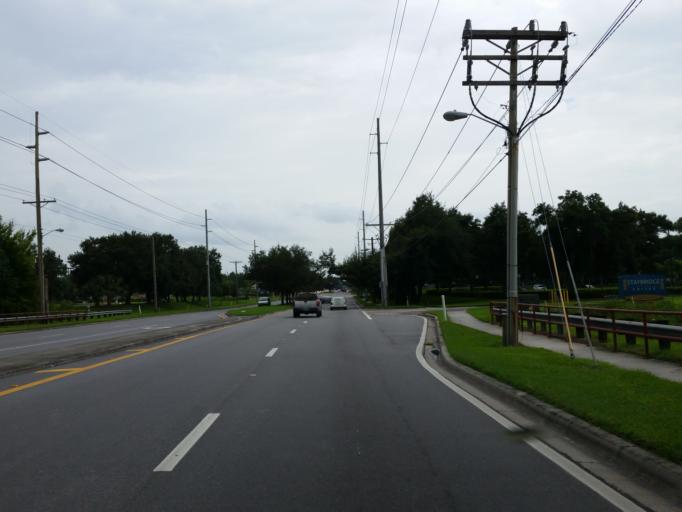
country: US
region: Florida
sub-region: Hillsborough County
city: Mango
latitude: 27.9786
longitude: -82.3352
